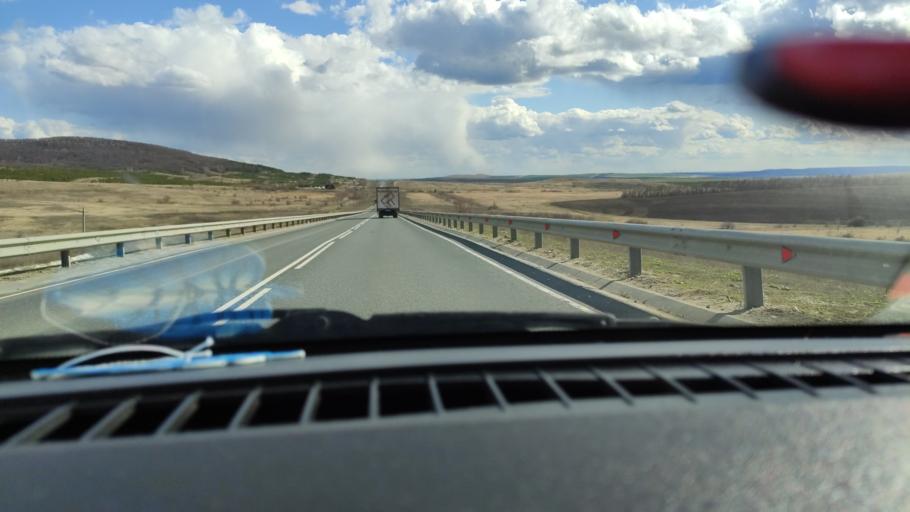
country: RU
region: Saratov
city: Alekseyevka
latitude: 52.3129
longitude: 47.9239
